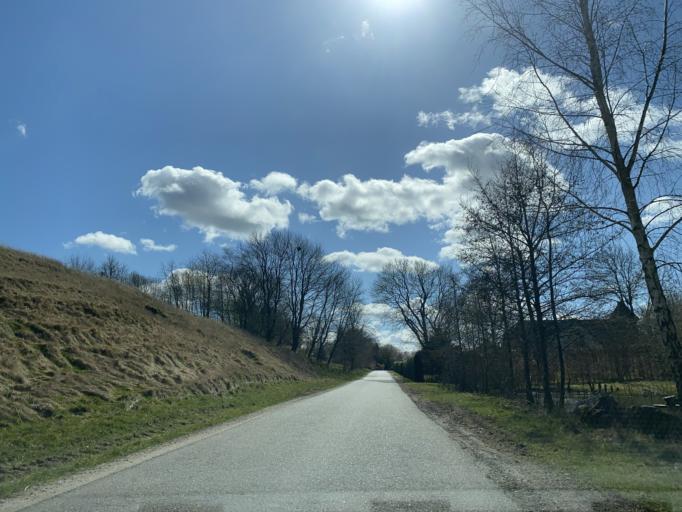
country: DK
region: Central Jutland
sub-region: Favrskov Kommune
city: Ulstrup
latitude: 56.3429
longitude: 9.7888
